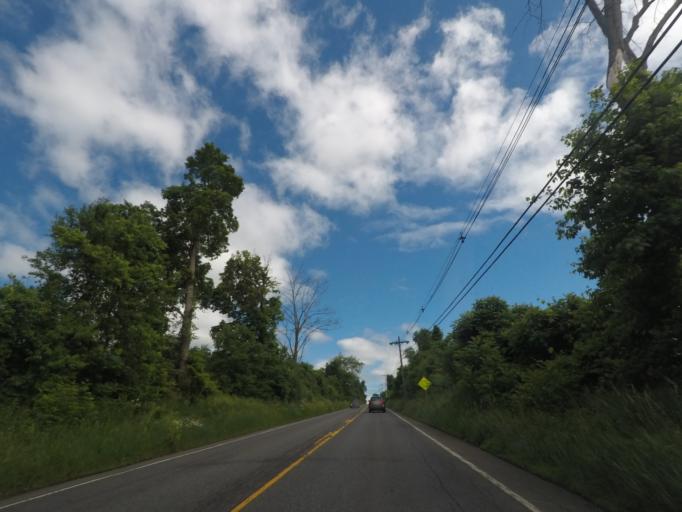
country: US
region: New York
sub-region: Columbia County
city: Philmont
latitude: 42.2179
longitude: -73.7087
